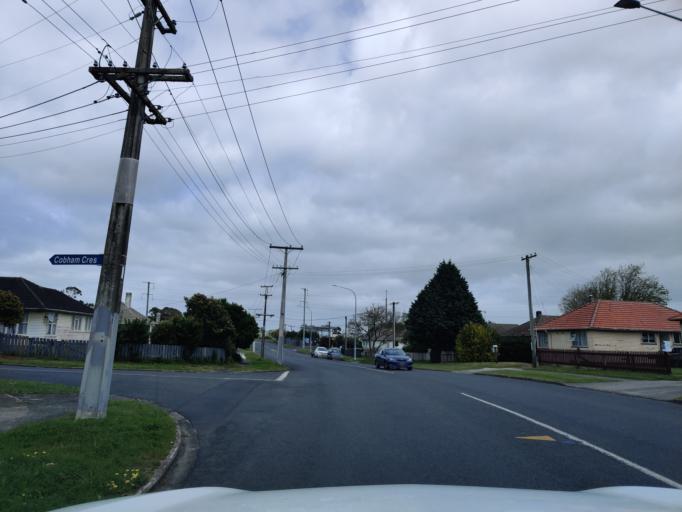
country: NZ
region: Waikato
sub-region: Waikato District
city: Ngaruawahia
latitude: -37.5658
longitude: 175.1497
